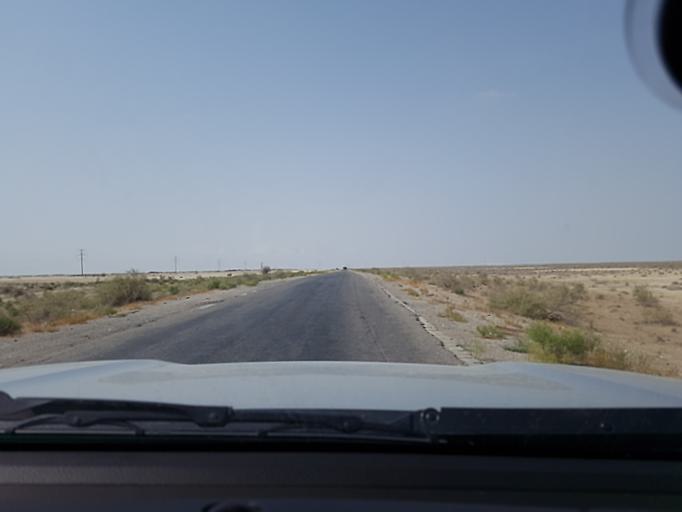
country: TM
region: Balkan
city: Gumdag
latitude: 38.7743
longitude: 54.5892
